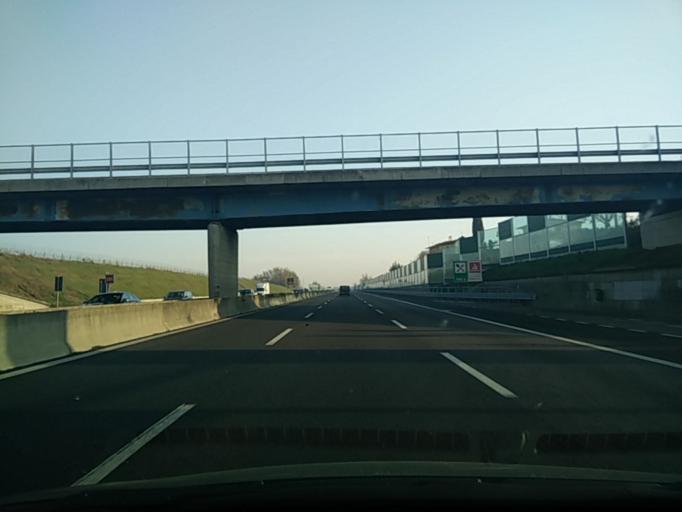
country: IT
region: Lombardy
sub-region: Provincia di Brescia
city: Adro
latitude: 45.6040
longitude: 9.9476
